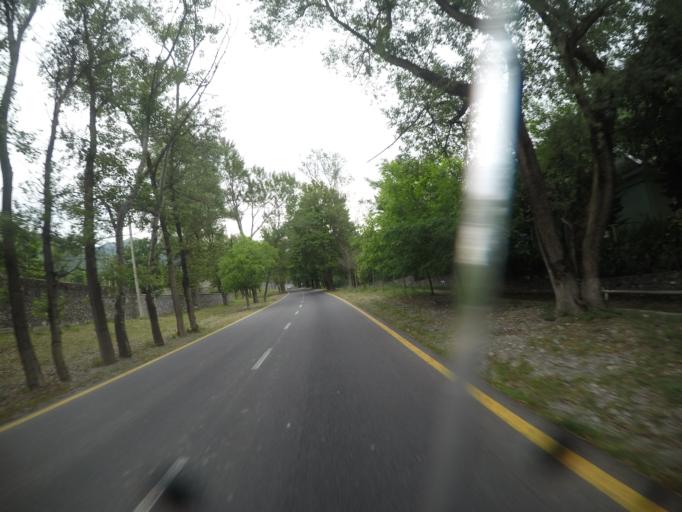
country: AZ
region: Shaki City
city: Sheki
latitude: 41.2391
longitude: 47.1844
